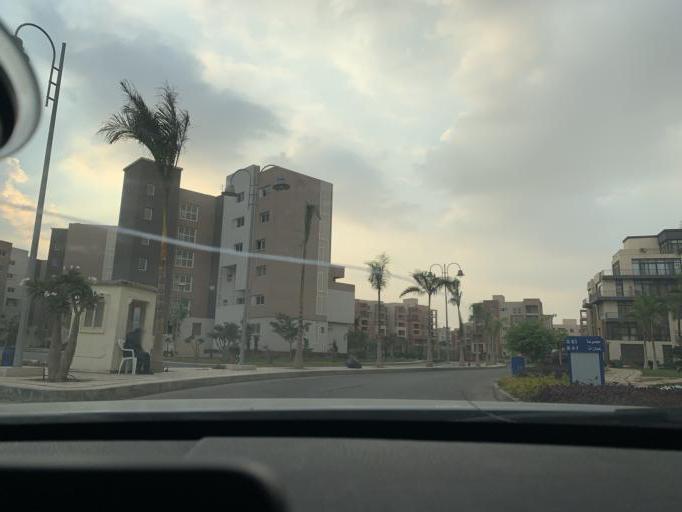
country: EG
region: Muhafazat al Qalyubiyah
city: Al Khankah
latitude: 30.1026
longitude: 31.6526
